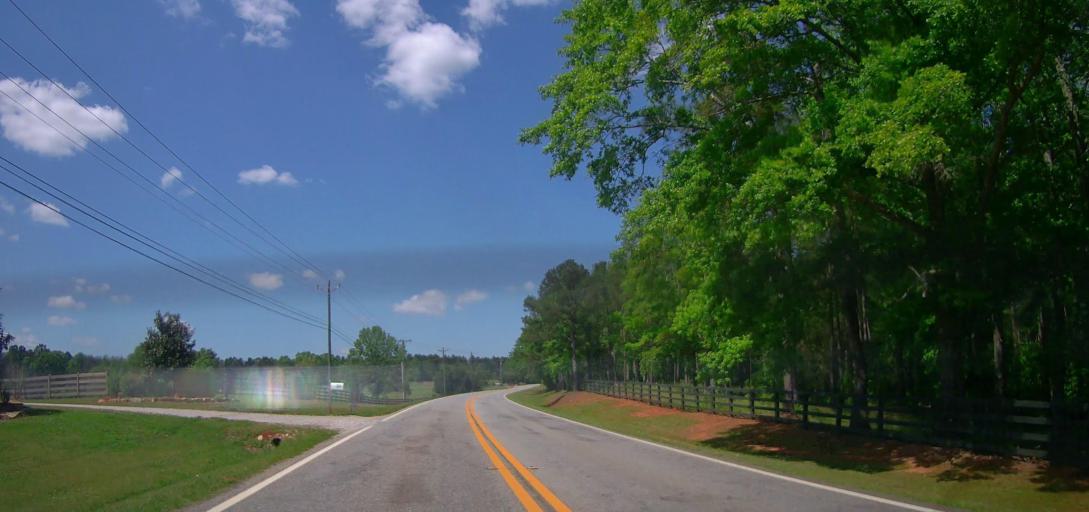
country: US
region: Georgia
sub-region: Putnam County
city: Eatonton
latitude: 33.2993
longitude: -83.3036
